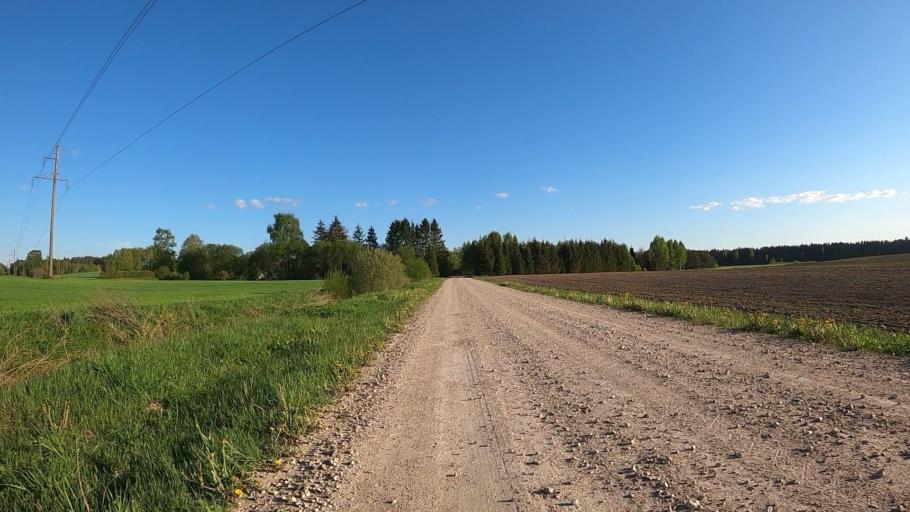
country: LV
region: Kekava
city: Kekava
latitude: 56.7693
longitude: 24.2874
